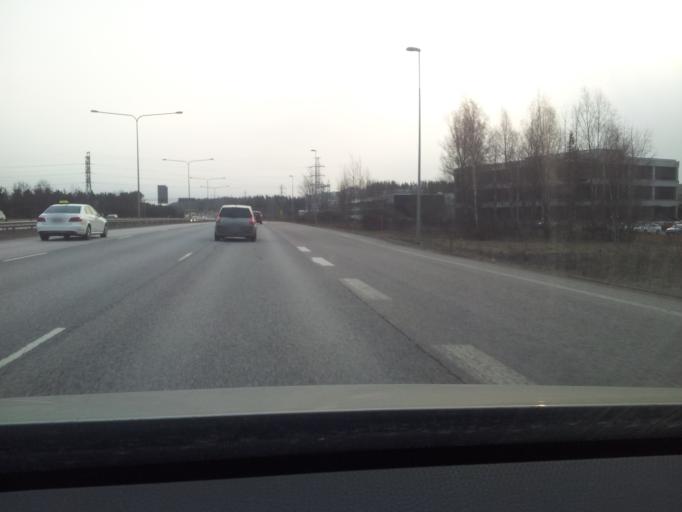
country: FI
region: Uusimaa
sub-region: Helsinki
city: Kilo
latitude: 60.2060
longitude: 24.7672
